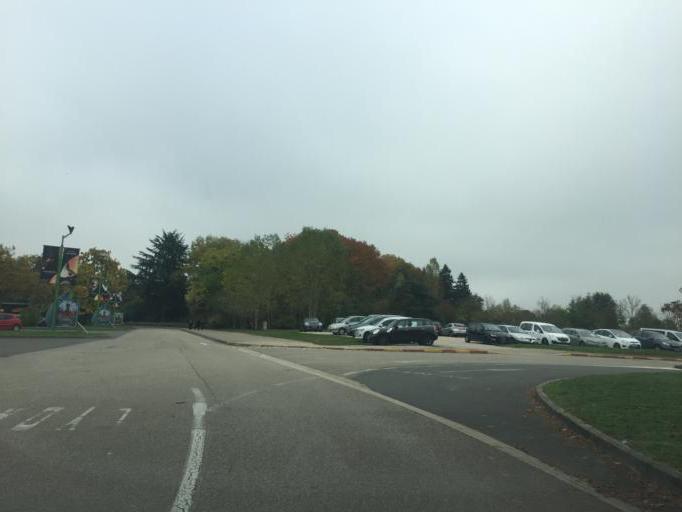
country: FR
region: Rhone-Alpes
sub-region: Departement de l'Ain
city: Villars-les-Dombes
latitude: 45.9918
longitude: 5.0249
